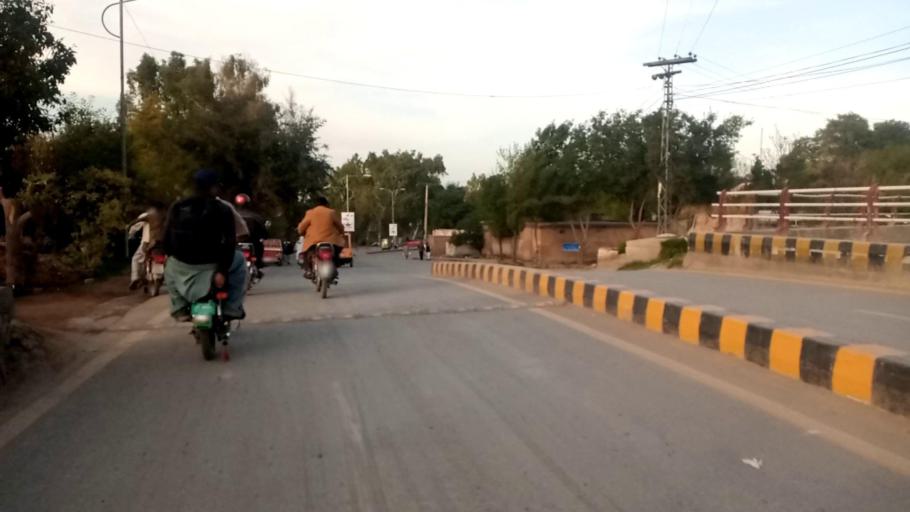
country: PK
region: Khyber Pakhtunkhwa
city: Peshawar
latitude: 34.0157
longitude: 71.5524
